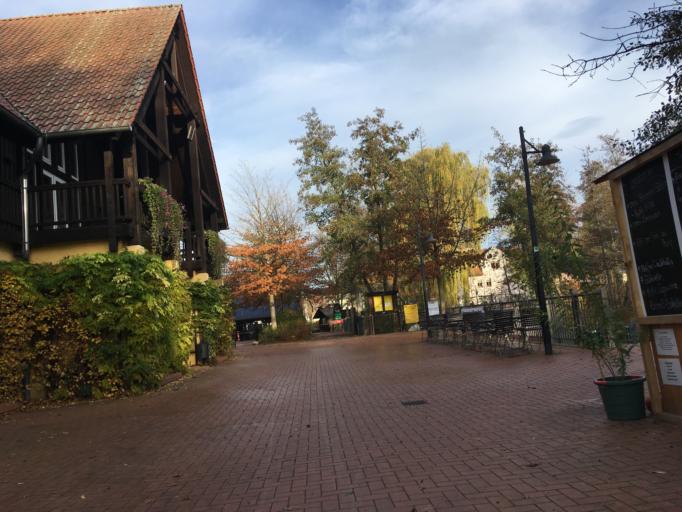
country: DE
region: Brandenburg
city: Luebben
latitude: 51.9387
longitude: 13.8975
